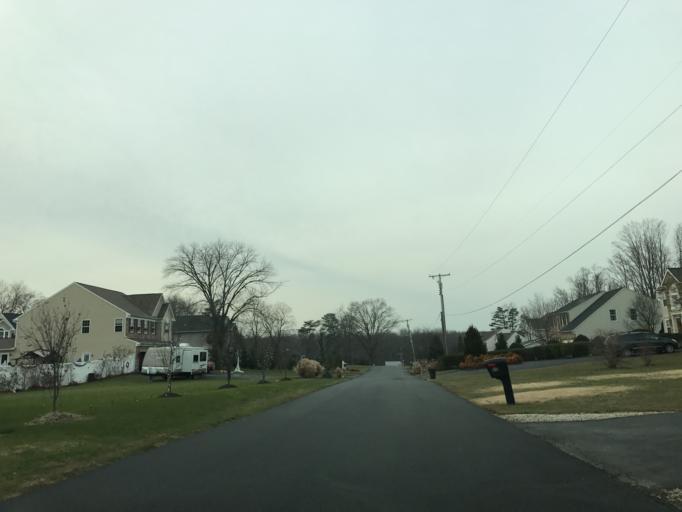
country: US
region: Maryland
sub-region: Baltimore County
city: White Marsh
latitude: 39.4087
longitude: -76.4077
